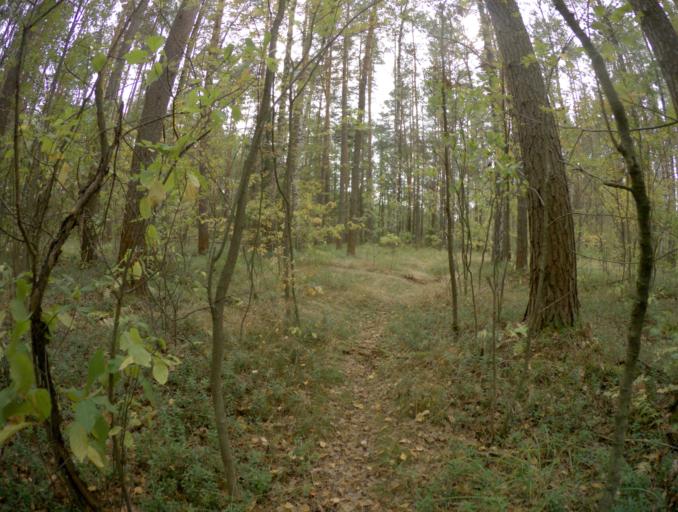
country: RU
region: Vladimir
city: Kommunar
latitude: 56.1314
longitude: 40.4974
